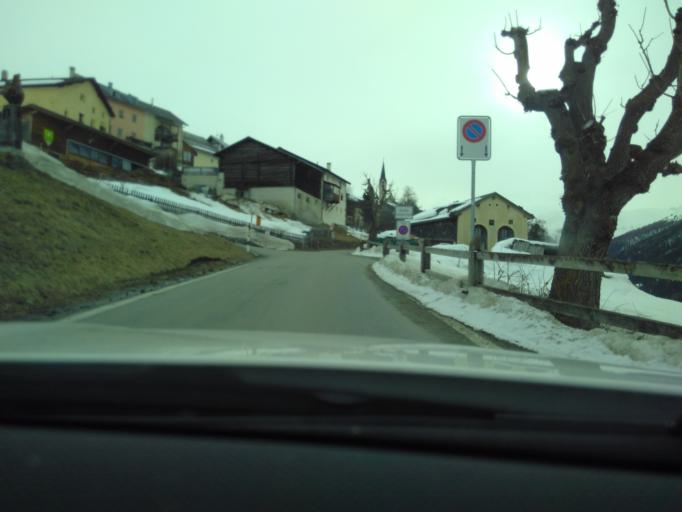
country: CH
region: Grisons
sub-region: Inn District
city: Zernez
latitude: 46.7756
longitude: 10.1489
